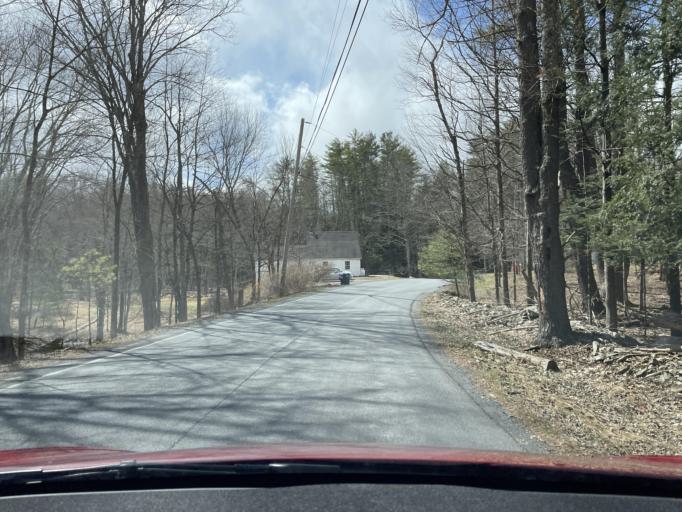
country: US
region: New York
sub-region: Ulster County
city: Zena
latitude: 42.0265
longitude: -74.0708
